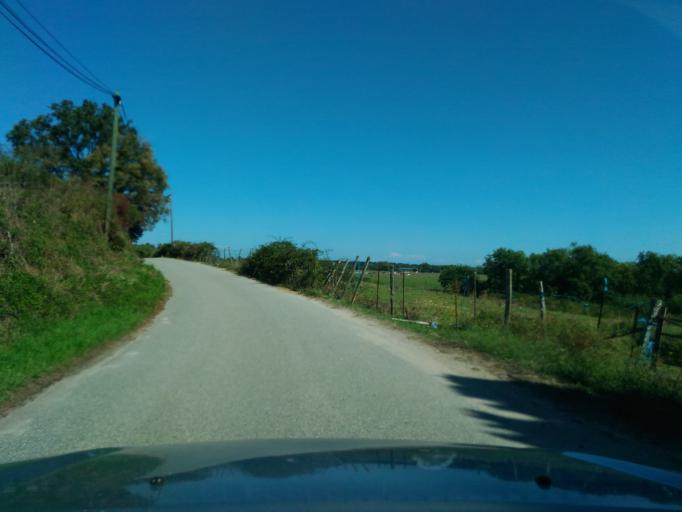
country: FR
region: Corsica
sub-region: Departement de la Haute-Corse
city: Aleria
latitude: 42.1044
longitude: 9.4753
